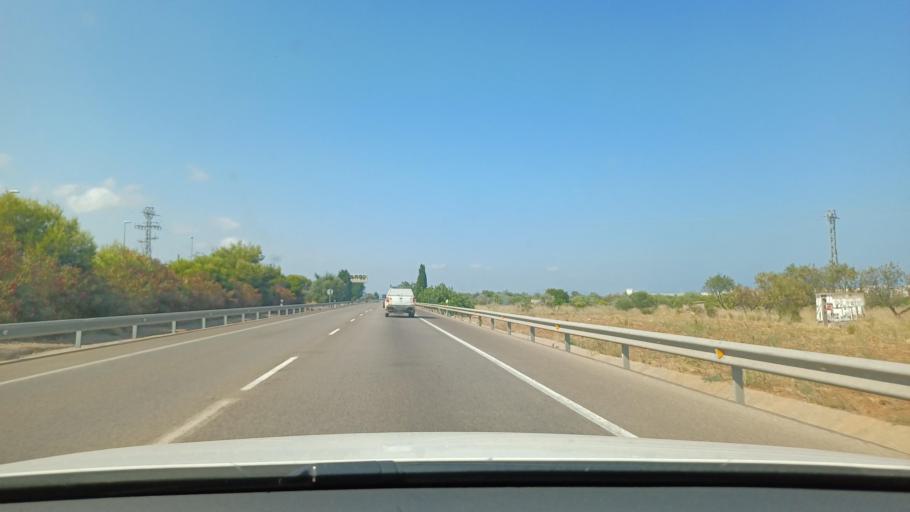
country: ES
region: Valencia
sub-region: Provincia de Castello
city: Orpesa/Oropesa del Mar
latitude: 40.1078
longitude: 0.1371
